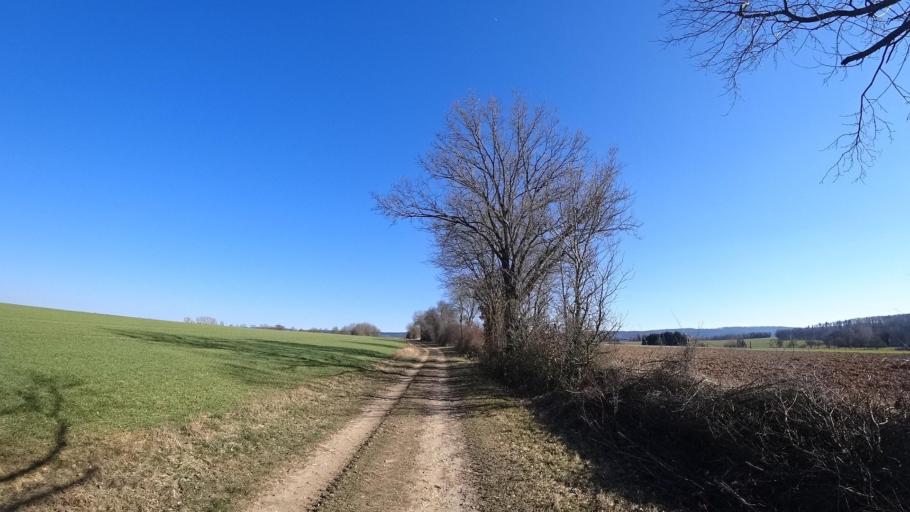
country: DE
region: Rheinland-Pfalz
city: Holzbach
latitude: 49.9569
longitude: 7.5349
